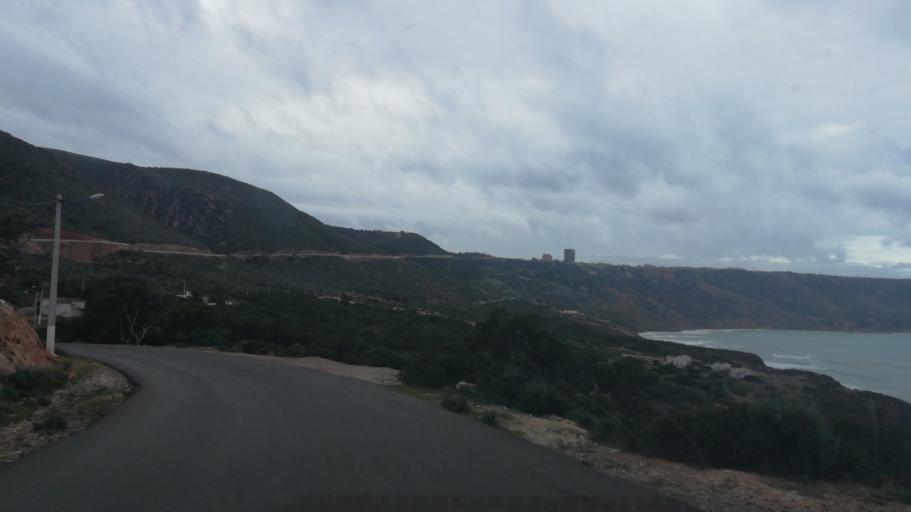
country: DZ
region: Oran
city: Bir el Djir
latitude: 35.7771
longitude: -0.5148
